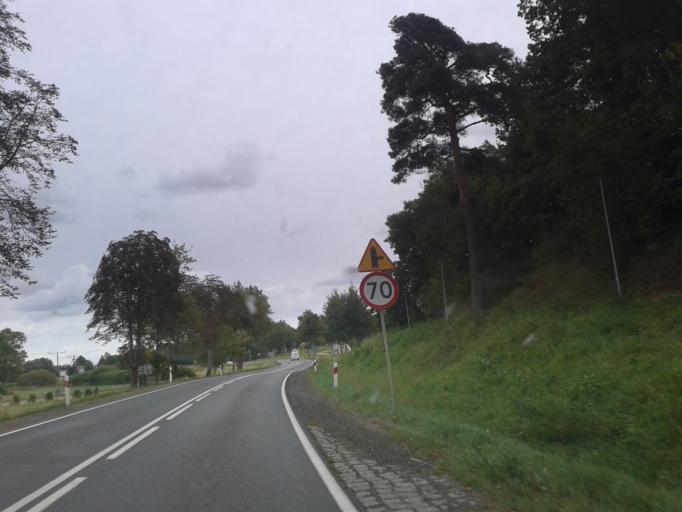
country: PL
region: West Pomeranian Voivodeship
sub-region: Powiat szczecinecki
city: Szczecinek
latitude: 53.7156
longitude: 16.7278
